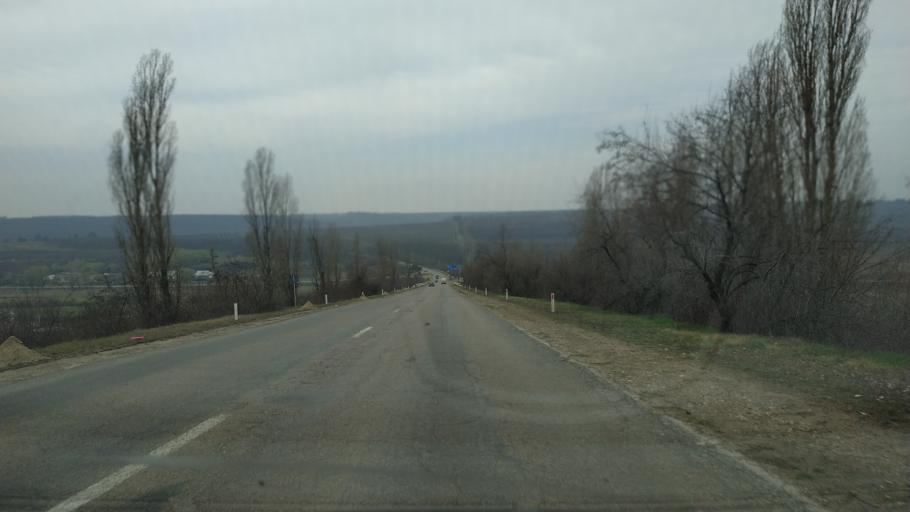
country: MD
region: Cahul
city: Cahul
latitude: 45.9558
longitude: 28.3535
